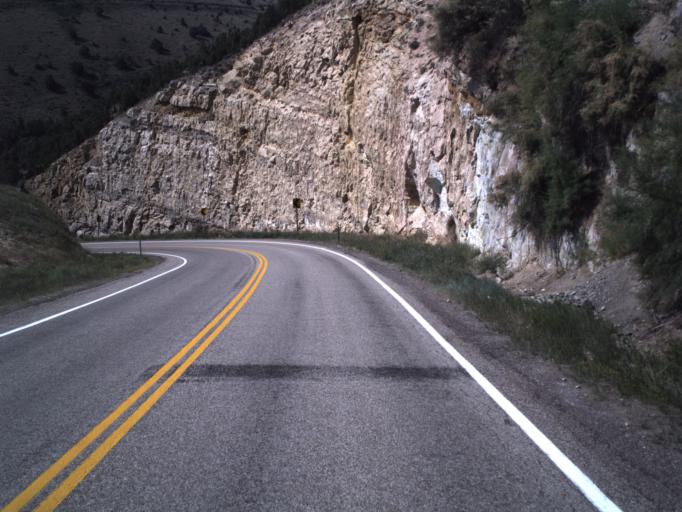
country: US
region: Utah
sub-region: Daggett County
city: Manila
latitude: 40.9092
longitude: -109.6957
